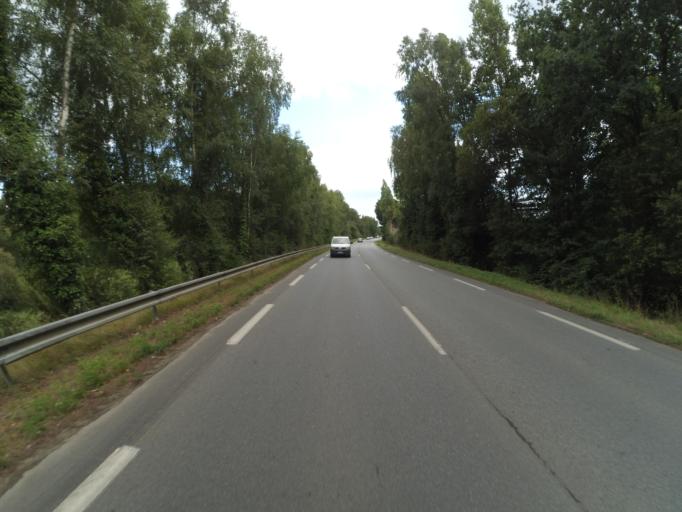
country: FR
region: Brittany
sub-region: Departement du Morbihan
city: Merlevenez
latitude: 47.7499
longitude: -3.2281
